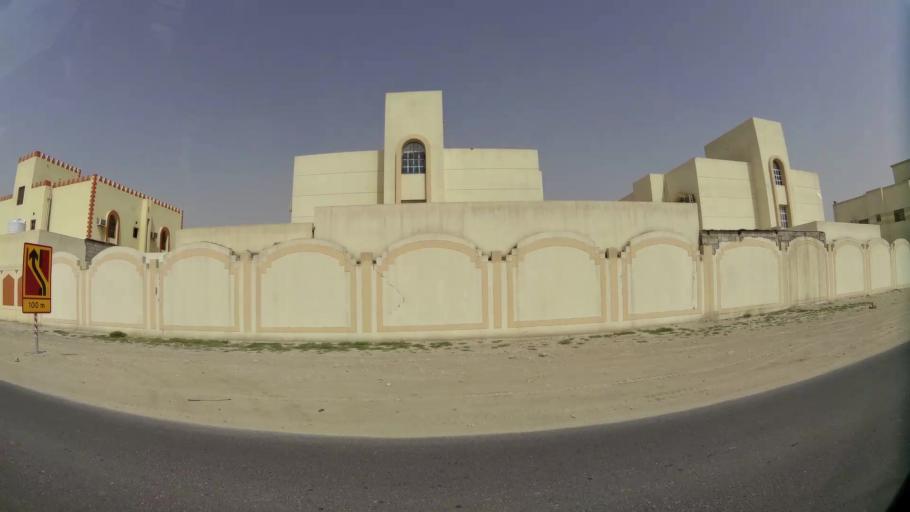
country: QA
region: Baladiyat ar Rayyan
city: Ar Rayyan
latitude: 25.2448
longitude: 51.3633
